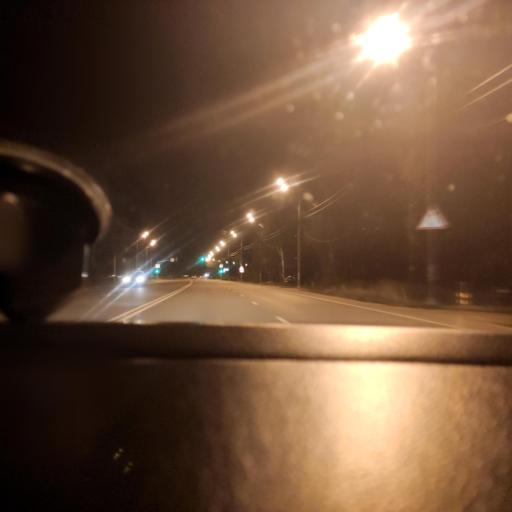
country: RU
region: Moskovskaya
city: Bronnitsy
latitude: 55.3986
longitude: 38.3143
